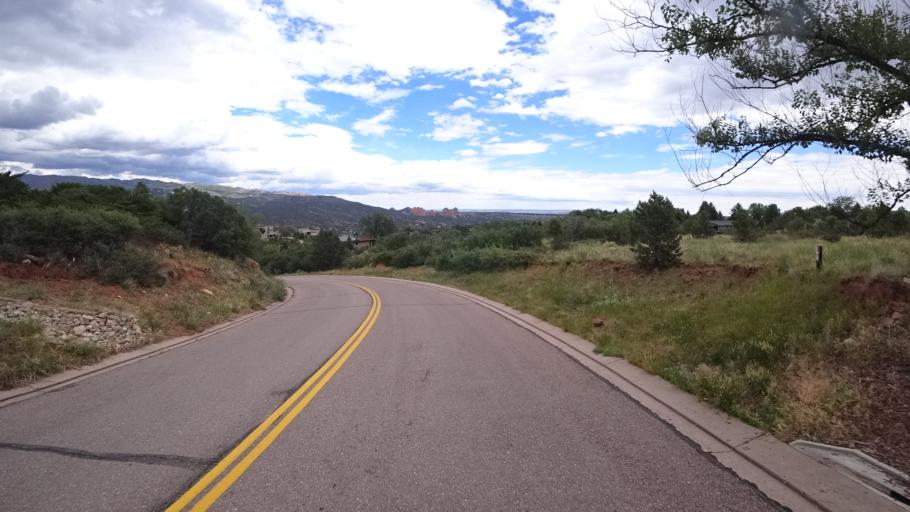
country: US
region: Colorado
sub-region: El Paso County
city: Manitou Springs
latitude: 38.8458
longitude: -104.8969
